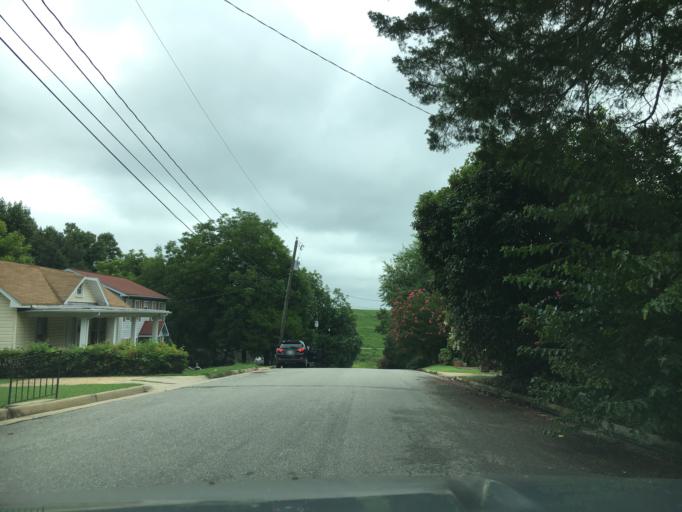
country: US
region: Virginia
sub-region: Halifax County
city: South Boston
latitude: 36.7167
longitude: -78.9010
